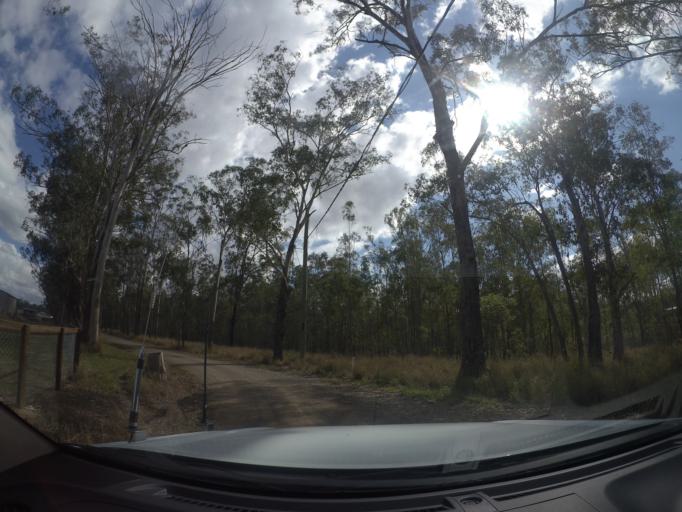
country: AU
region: Queensland
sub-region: Logan
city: North Maclean
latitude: -27.8072
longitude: 152.9937
